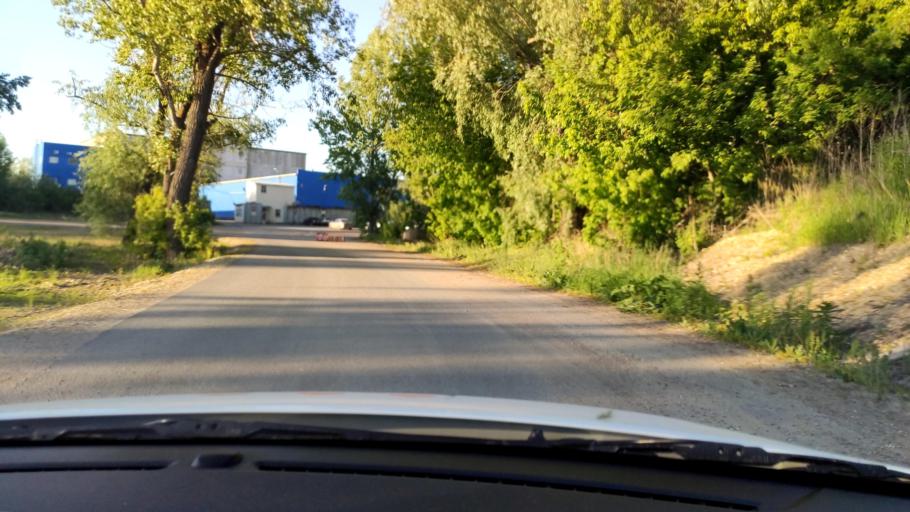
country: RU
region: Tatarstan
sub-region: Gorod Kazan'
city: Kazan
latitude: 55.8028
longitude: 49.0508
